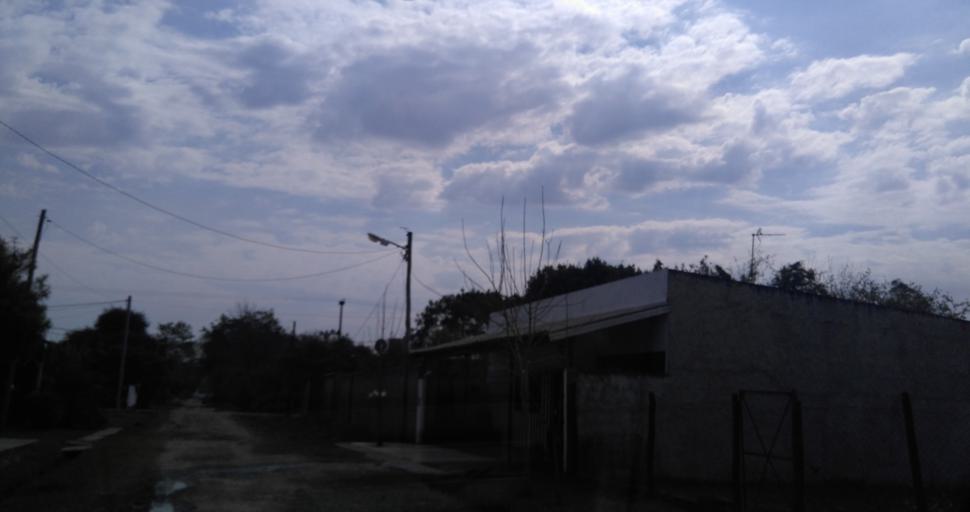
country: AR
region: Chaco
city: Fontana
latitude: -27.4520
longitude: -59.0364
